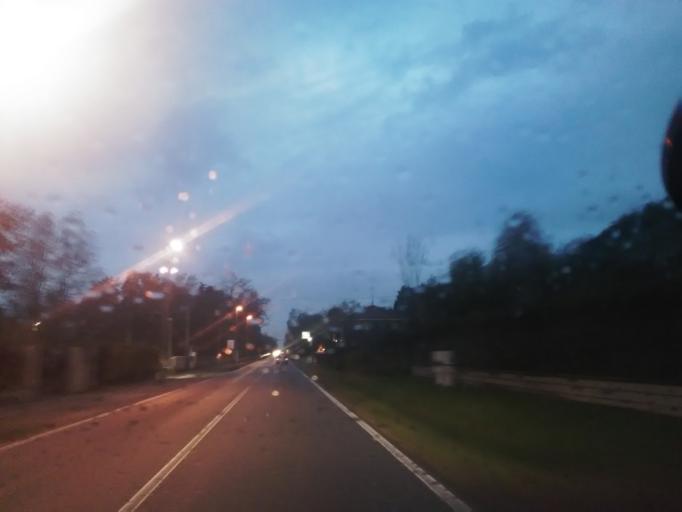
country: IT
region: Piedmont
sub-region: Provincia di Vercelli
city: Gattinara
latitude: 45.6111
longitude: 8.3437
